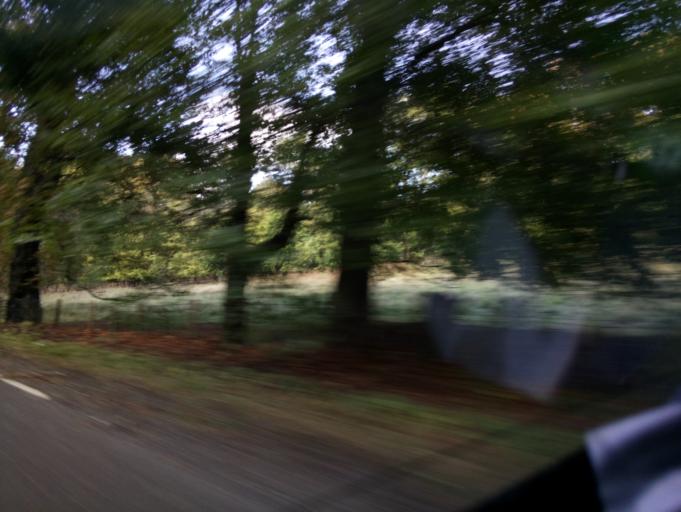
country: GB
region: England
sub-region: Hampshire
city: Alton
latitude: 51.1601
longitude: -1.0104
